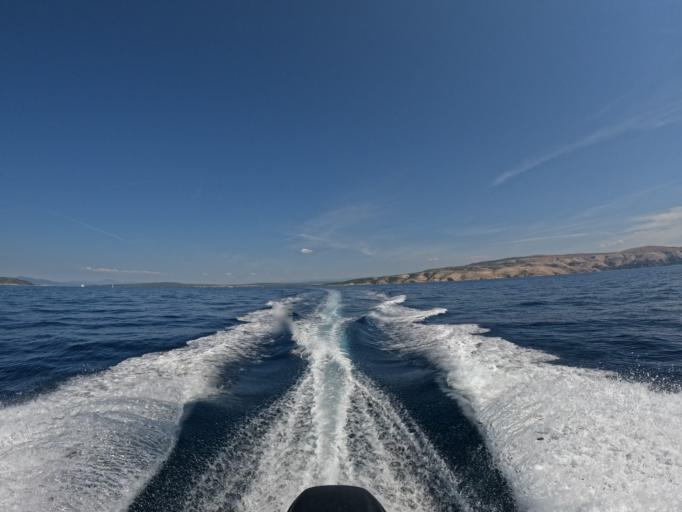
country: HR
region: Primorsko-Goranska
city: Punat
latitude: 44.9343
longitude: 14.6164
